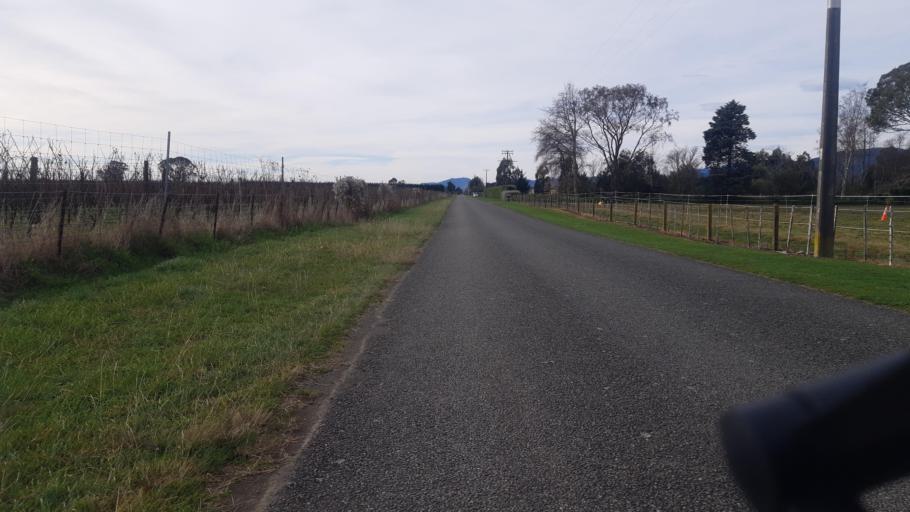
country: NZ
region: Tasman
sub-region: Tasman District
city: Brightwater
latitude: -41.3566
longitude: 173.1238
